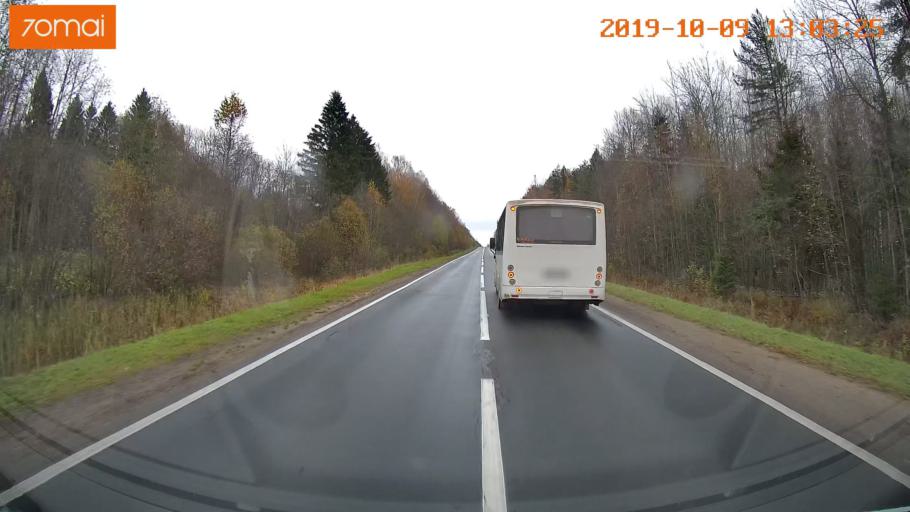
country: RU
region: Jaroslavl
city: Lyubim
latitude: 58.3595
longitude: 40.5256
